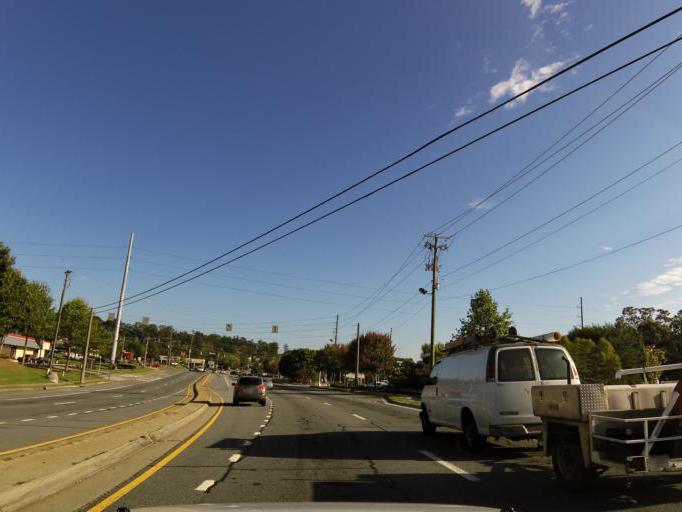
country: US
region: Georgia
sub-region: Cobb County
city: Marietta
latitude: 33.9445
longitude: -84.6242
